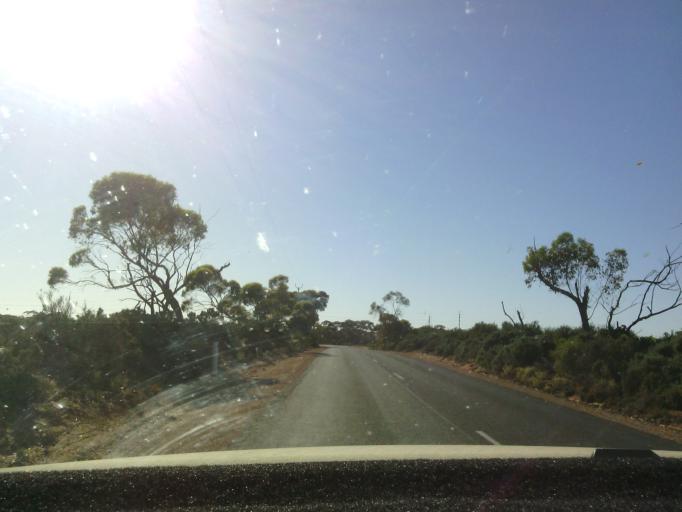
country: AU
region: South Australia
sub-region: Berri and Barmera
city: Berri
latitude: -34.2540
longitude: 140.5914
